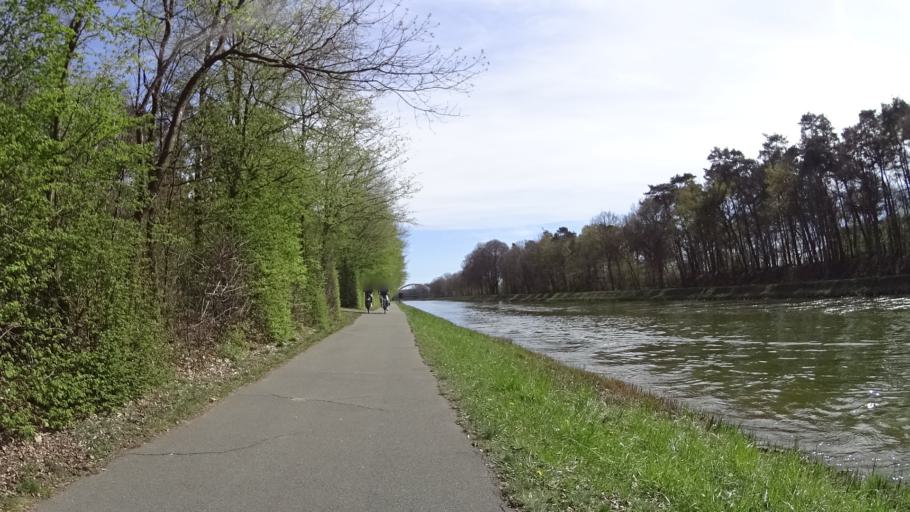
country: DE
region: North Rhine-Westphalia
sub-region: Regierungsbezirk Munster
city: Dreierwalde
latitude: 52.3198
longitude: 7.4596
